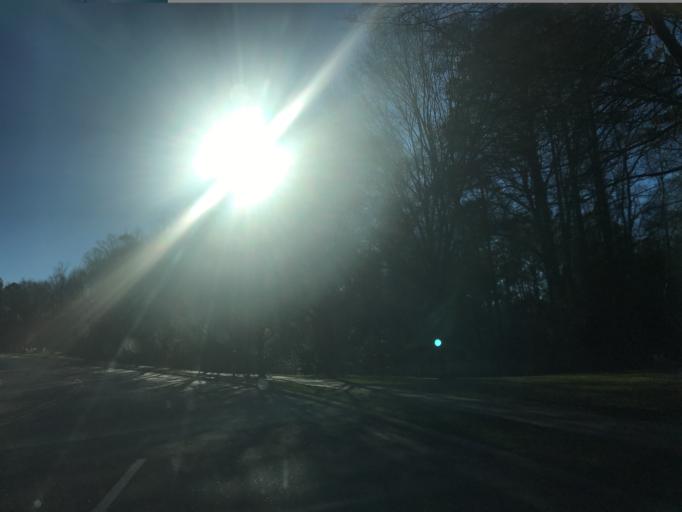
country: US
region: North Carolina
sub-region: Wake County
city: West Raleigh
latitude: 35.8314
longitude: -78.6926
